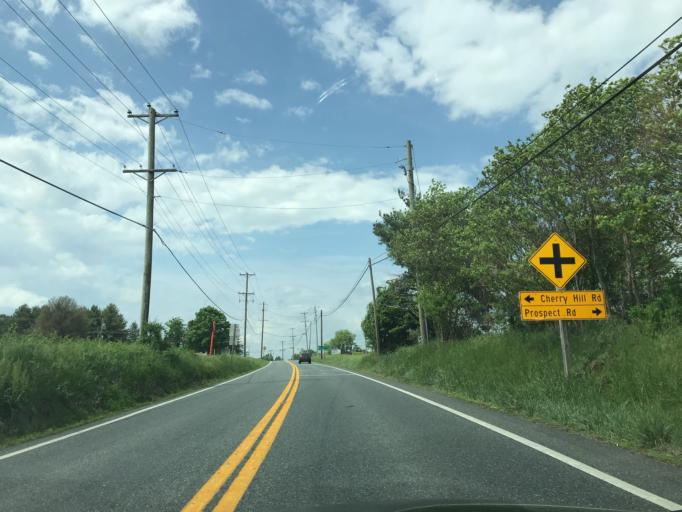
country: US
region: Maryland
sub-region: Harford County
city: Bel Air North
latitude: 39.6504
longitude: -76.3349
